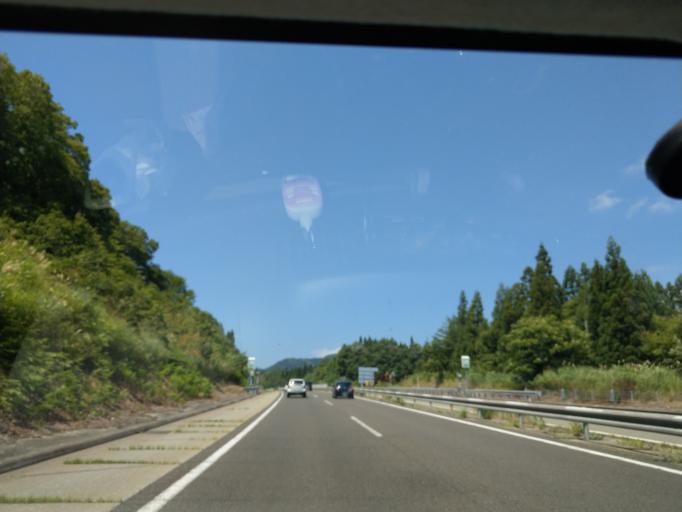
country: JP
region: Akita
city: Omagari
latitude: 39.4210
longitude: 140.4341
